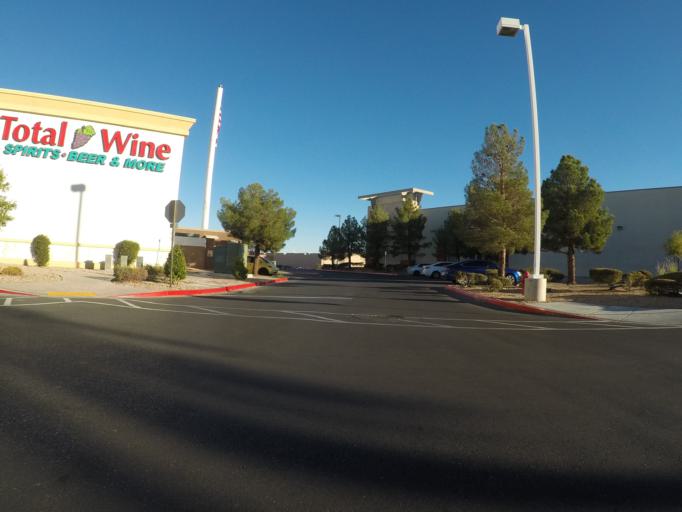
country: US
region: Nevada
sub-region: Clark County
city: Summerlin South
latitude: 36.1629
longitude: -115.2890
